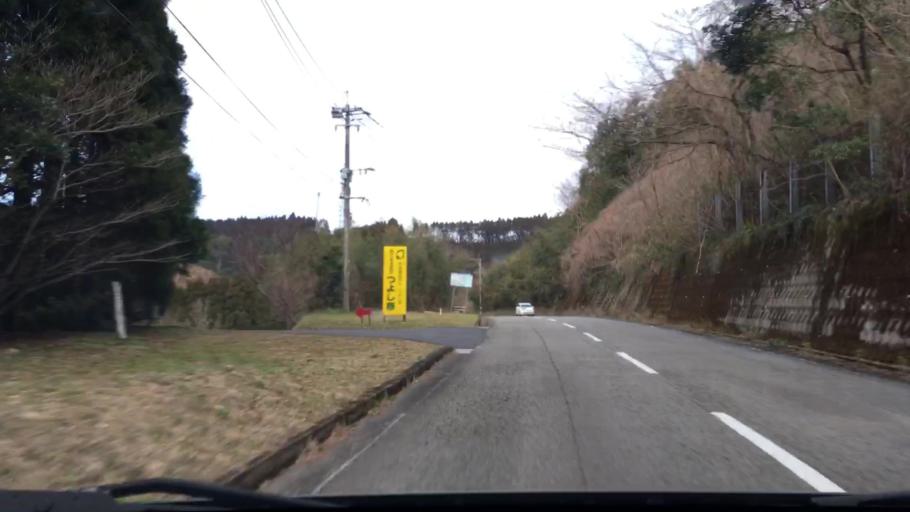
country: JP
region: Miyazaki
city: Nichinan
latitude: 31.6643
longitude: 131.3174
